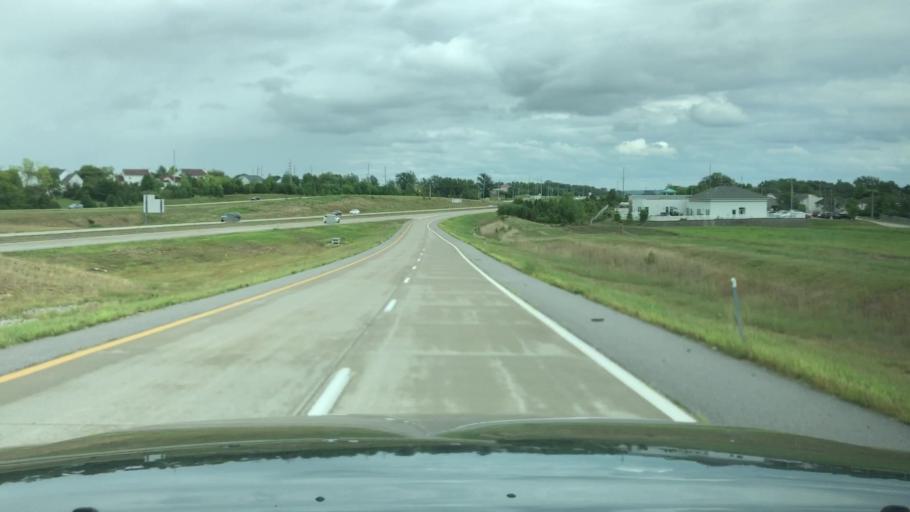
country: US
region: Missouri
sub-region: Saint Charles County
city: Dardenne Prairie
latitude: 38.7673
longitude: -90.7415
